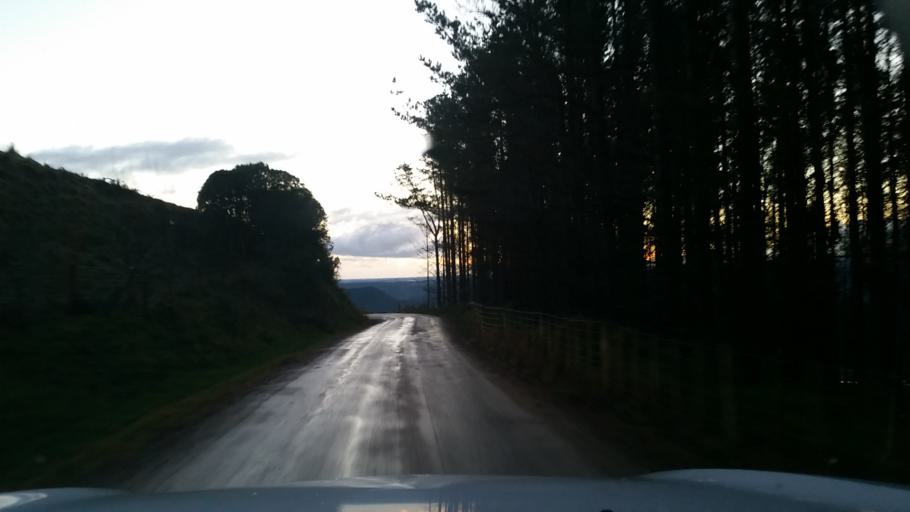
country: NZ
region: Manawatu-Wanganui
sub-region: Wanganui District
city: Wanganui
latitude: -39.7736
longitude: 174.8637
